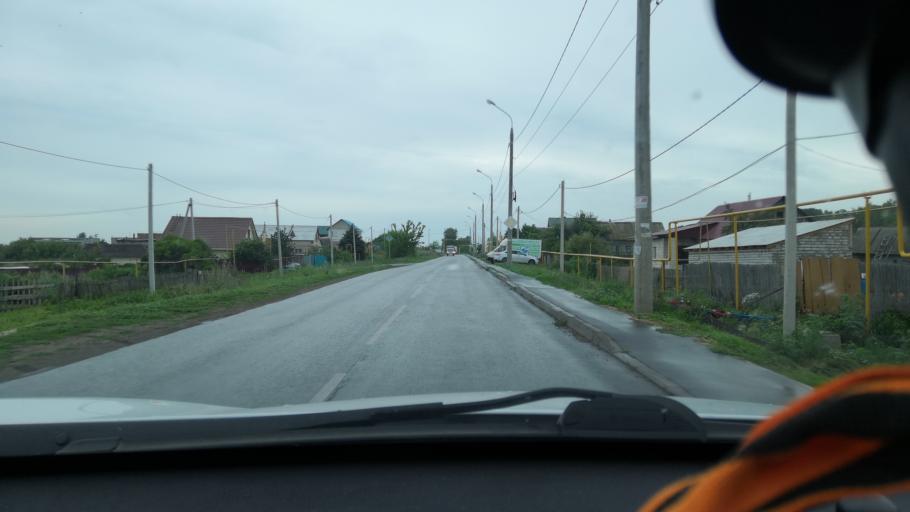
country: RU
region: Samara
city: Novosemeykino
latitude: 53.3805
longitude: 50.3497
